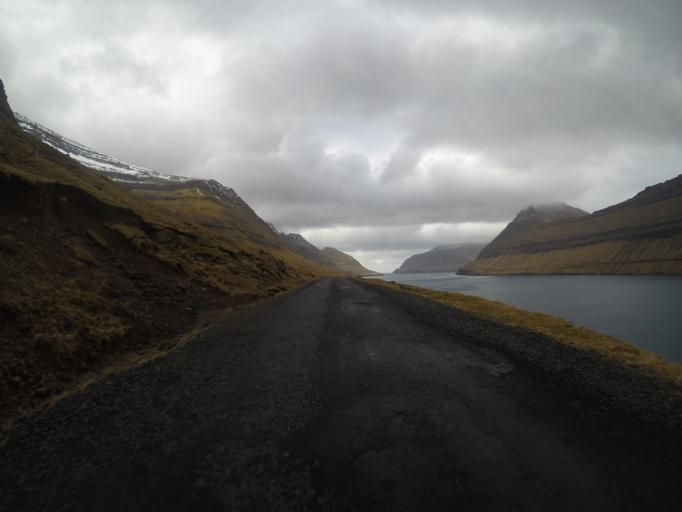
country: FO
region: Nordoyar
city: Klaksvik
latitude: 62.3135
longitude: -6.5512
